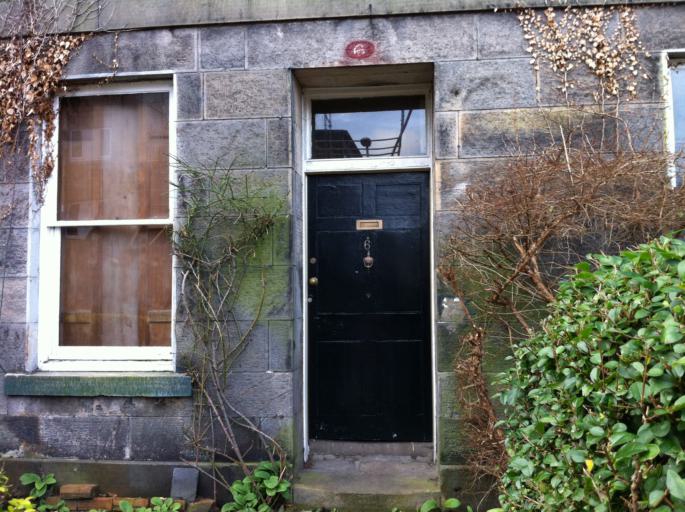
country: GB
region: Scotland
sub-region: Edinburgh
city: Edinburgh
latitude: 55.9592
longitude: -3.2100
